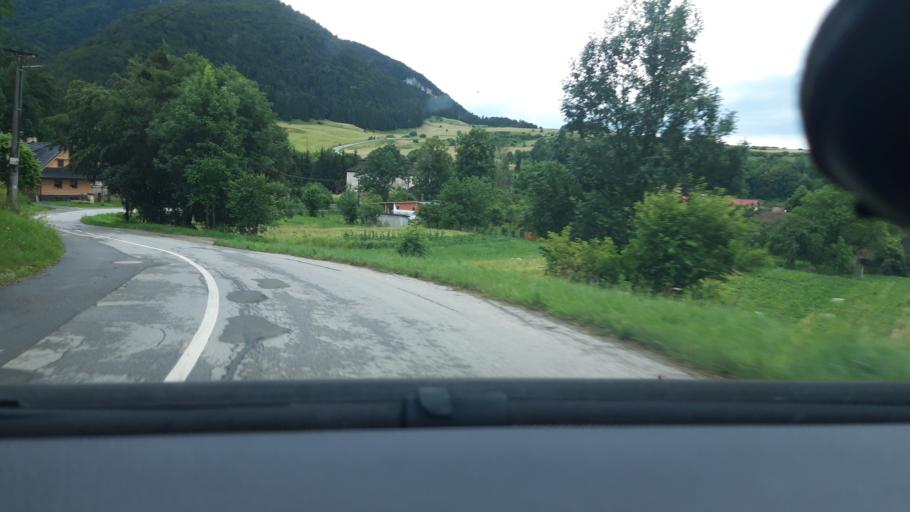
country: SK
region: Zilinsky
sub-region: Okres Martin
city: Martin
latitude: 48.9883
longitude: 18.9689
